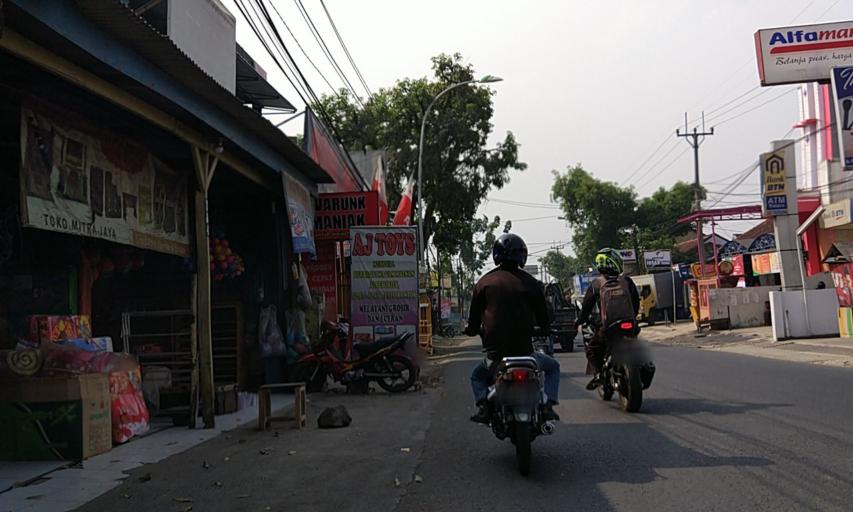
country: ID
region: West Java
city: Soreang
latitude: -7.0153
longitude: 107.5487
